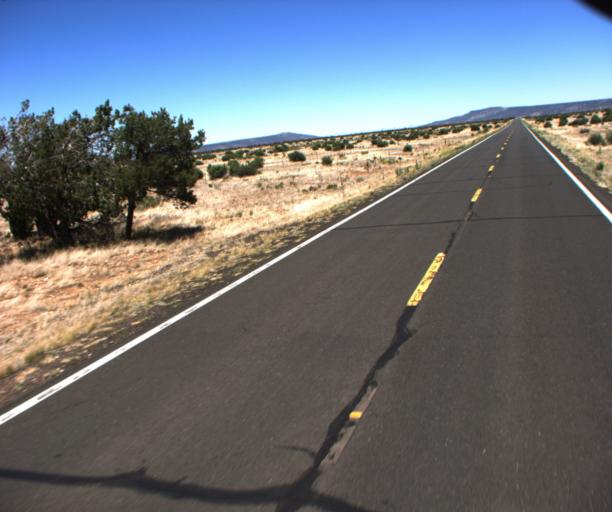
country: US
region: Arizona
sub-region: Coconino County
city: LeChee
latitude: 34.7515
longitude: -111.0371
